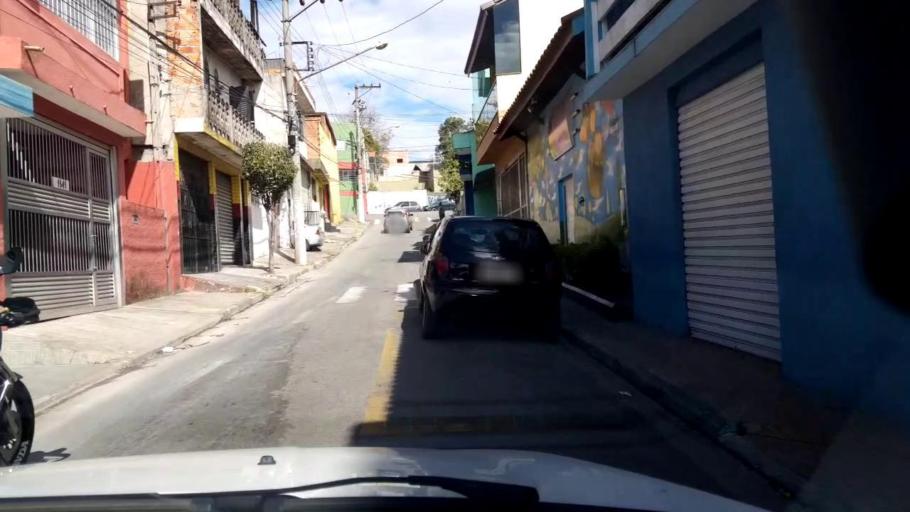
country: BR
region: Sao Paulo
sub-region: Ferraz De Vasconcelos
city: Ferraz de Vasconcelos
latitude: -23.5313
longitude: -46.3922
